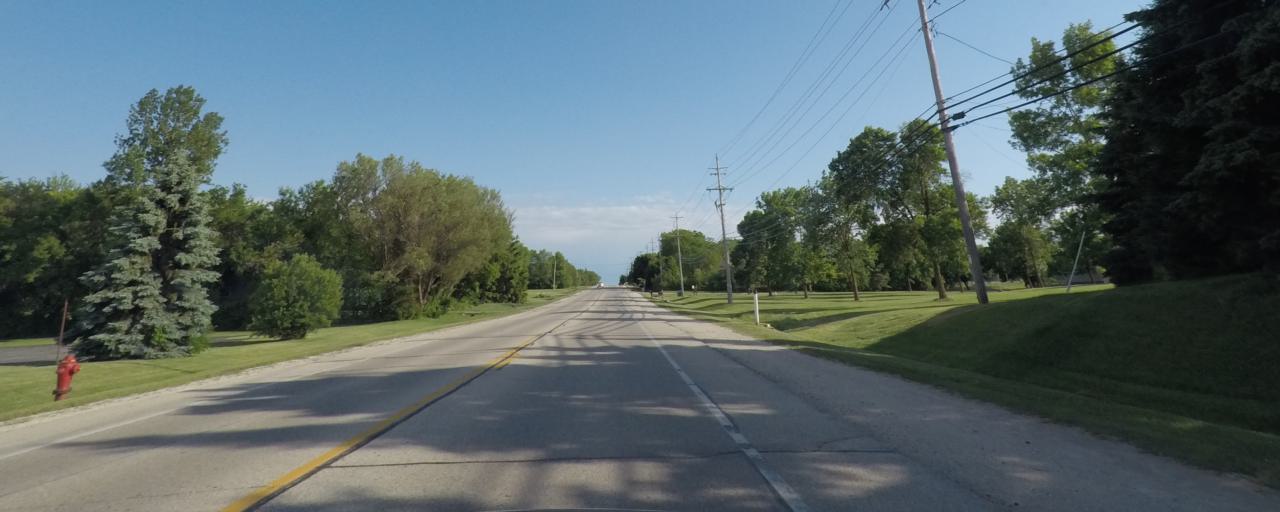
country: US
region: Wisconsin
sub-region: Waukesha County
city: New Berlin
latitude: 42.9538
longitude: -88.0893
